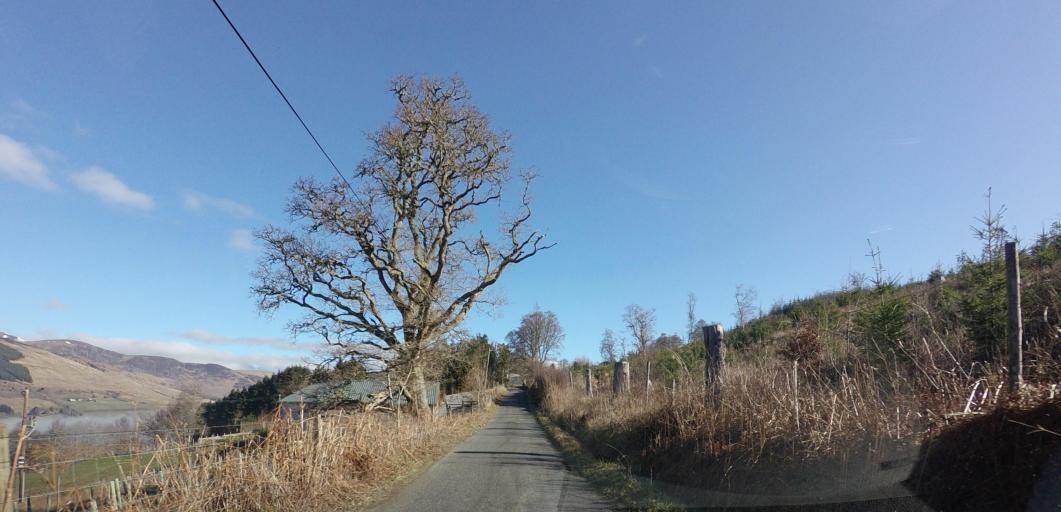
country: GB
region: Scotland
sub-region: Perth and Kinross
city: Comrie
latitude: 56.5541
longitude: -4.0863
